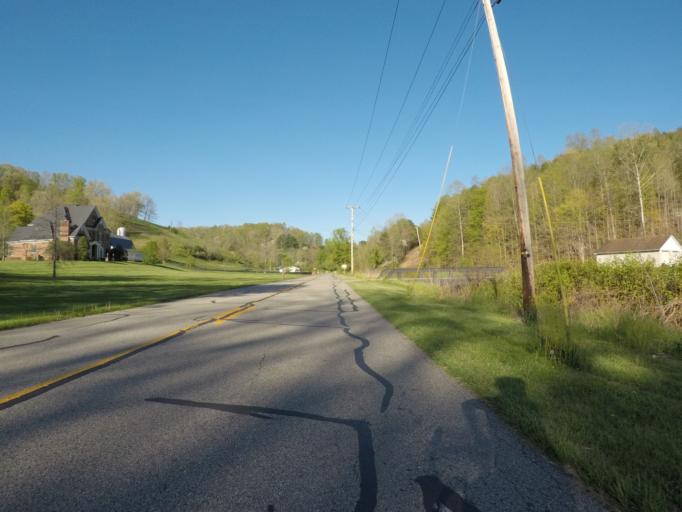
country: US
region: Kentucky
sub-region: Boyd County
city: Meads
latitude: 38.3651
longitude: -82.6865
